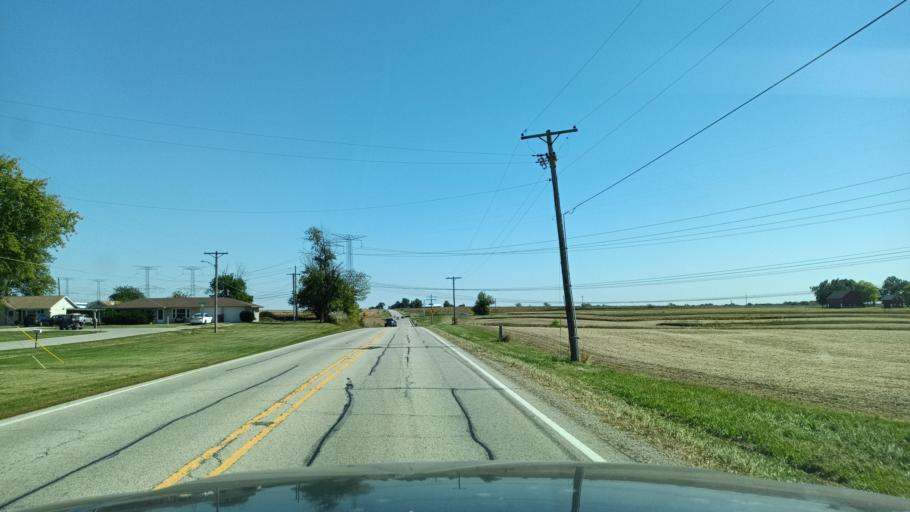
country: US
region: Illinois
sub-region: Tazewell County
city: Morton
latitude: 40.6138
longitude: -89.4087
